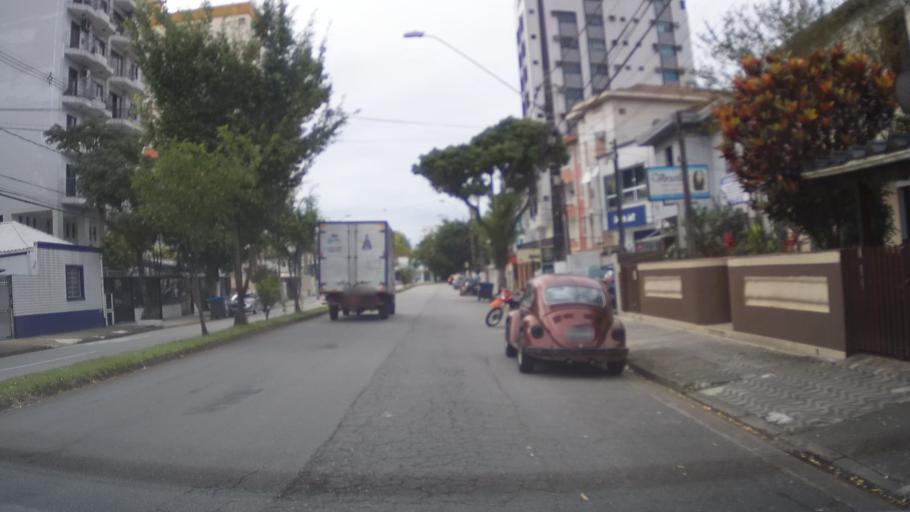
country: BR
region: Sao Paulo
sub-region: Santos
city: Santos
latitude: -23.9643
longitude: -46.3177
